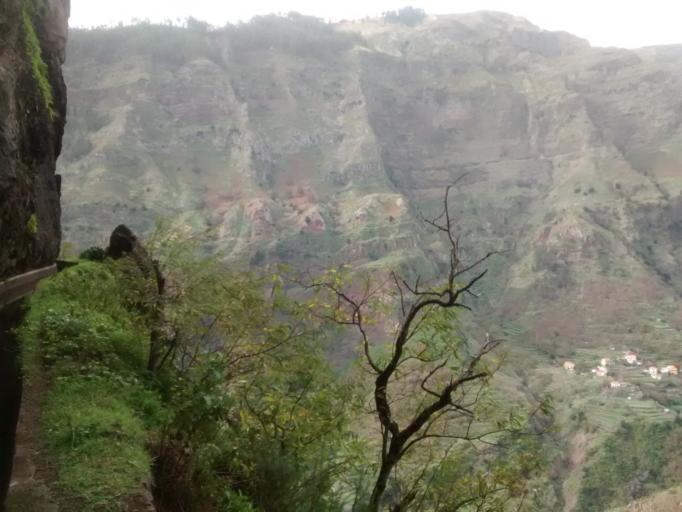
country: PT
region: Madeira
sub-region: Ribeira Brava
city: Campanario
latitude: 32.7159
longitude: -17.0263
